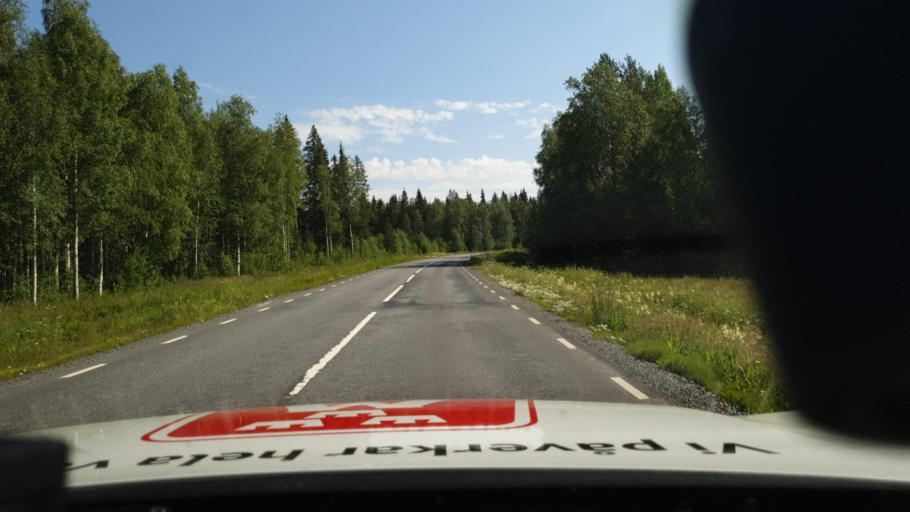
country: SE
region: Norrbotten
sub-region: Lulea Kommun
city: Gammelstad
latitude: 65.7894
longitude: 22.1151
